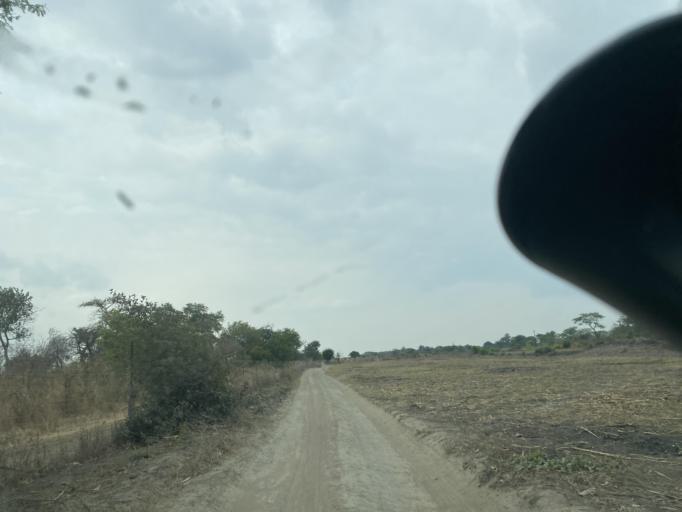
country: ZM
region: Lusaka
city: Lusaka
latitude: -15.2509
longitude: 28.3315
